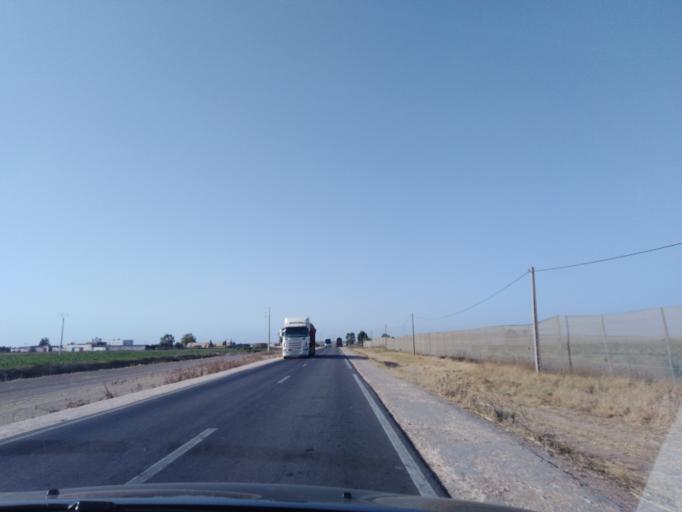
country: MA
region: Doukkala-Abda
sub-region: Safi
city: Youssoufia
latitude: 32.5154
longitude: -8.7429
